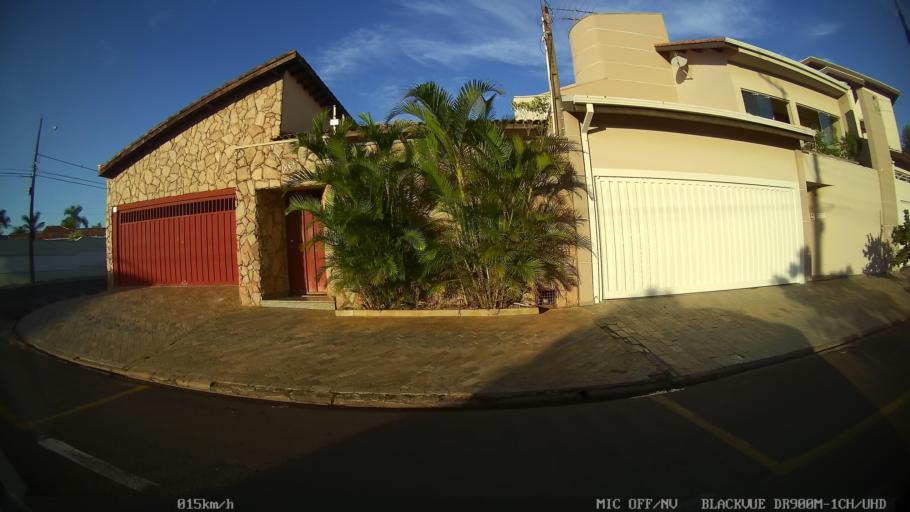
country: BR
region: Sao Paulo
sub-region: Franca
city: Franca
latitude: -20.5339
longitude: -47.3864
